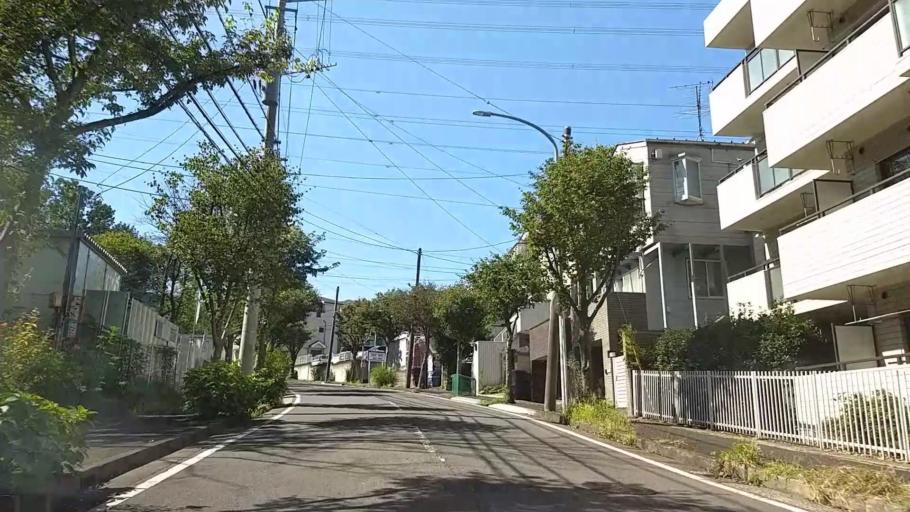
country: JP
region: Tokyo
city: Chofugaoka
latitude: 35.5709
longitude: 139.5381
